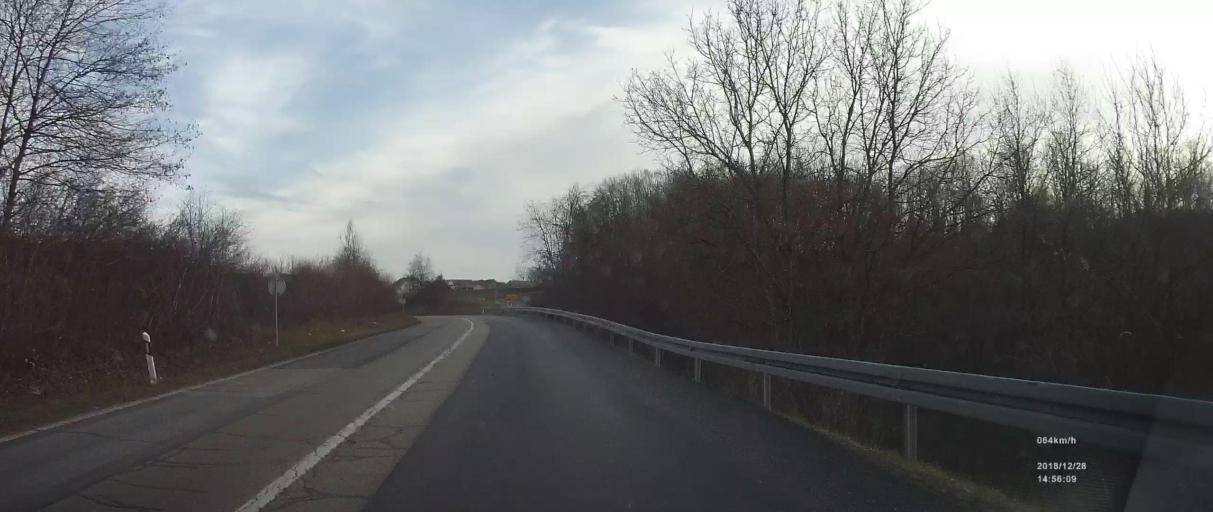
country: HR
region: Karlovacka
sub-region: Grad Karlovac
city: Karlovac
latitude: 45.4536
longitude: 15.4415
